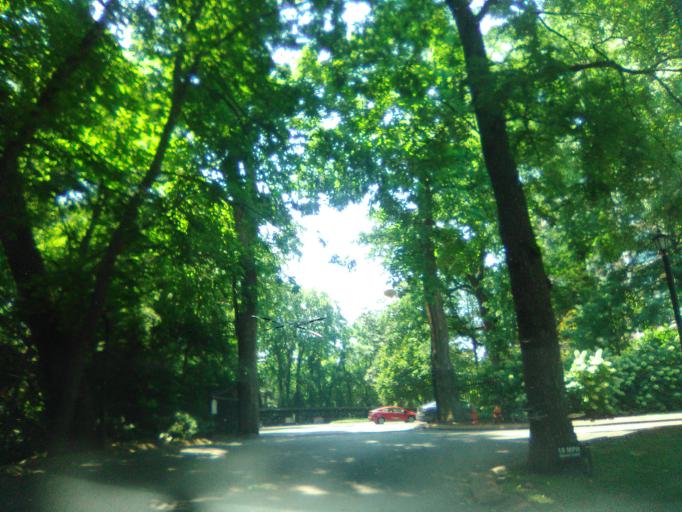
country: US
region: Tennessee
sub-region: Davidson County
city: Belle Meade
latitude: 36.1287
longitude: -86.8408
